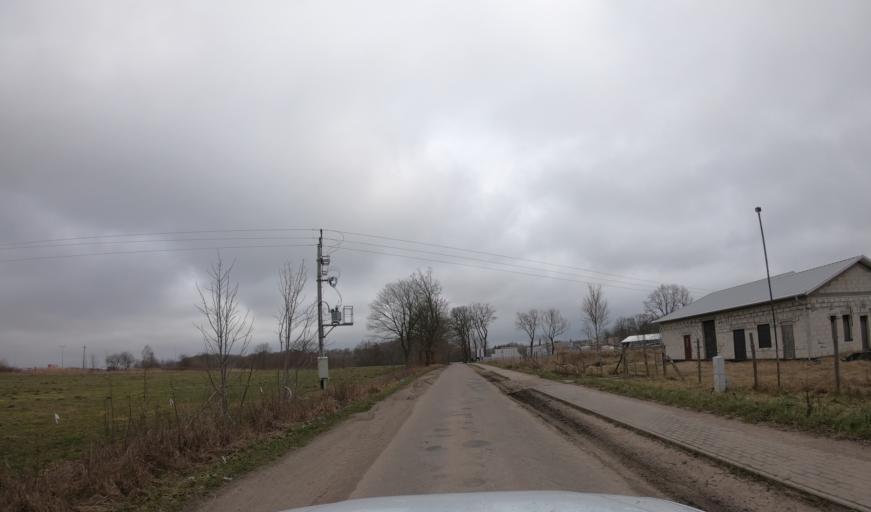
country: PL
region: West Pomeranian Voivodeship
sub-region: Powiat gryficki
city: Cerkwica
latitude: 54.0037
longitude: 15.1044
